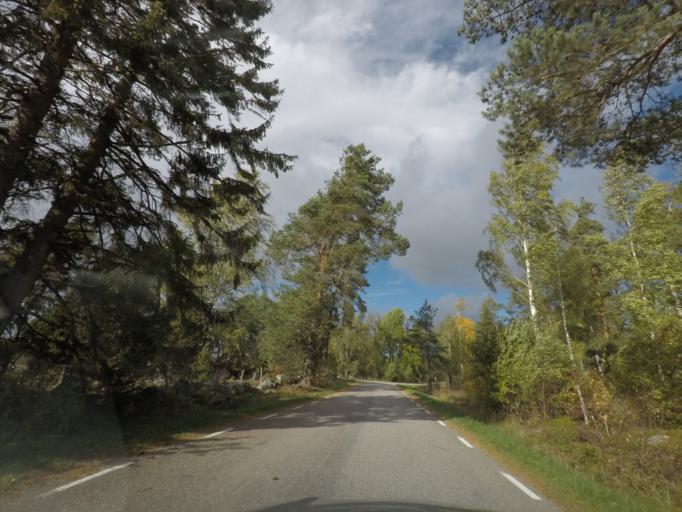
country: SE
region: Soedermanland
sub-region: Eskilstuna Kommun
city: Kvicksund
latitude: 59.3174
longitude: 16.2702
